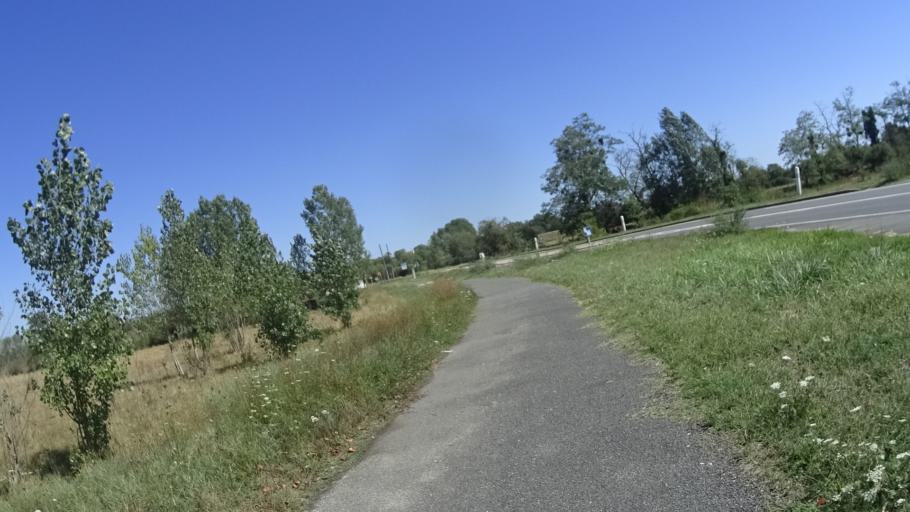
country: FR
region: Centre
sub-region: Departement du Loiret
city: Bonny-sur-Loire
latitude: 47.5518
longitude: 2.8398
